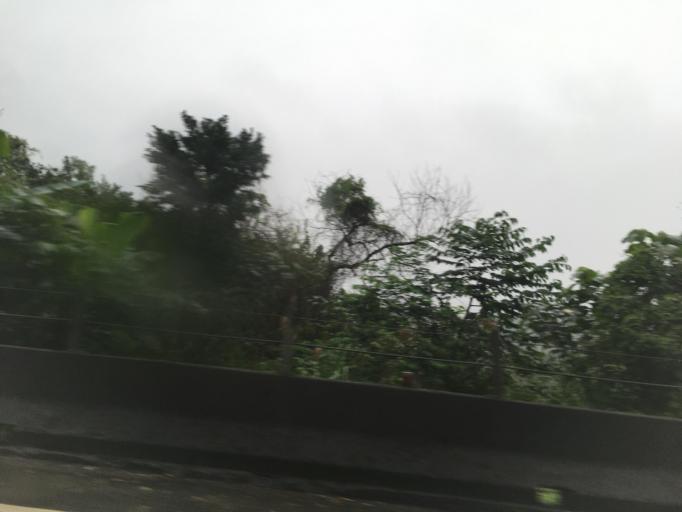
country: TW
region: Taiwan
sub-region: Keelung
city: Keelung
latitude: 25.0209
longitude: 121.8966
